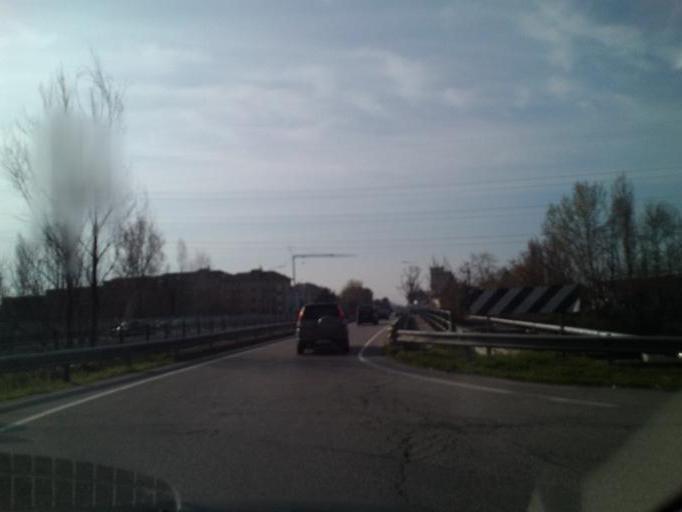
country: IT
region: Lombardy
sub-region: Provincia di Mantova
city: Sant'Antonio
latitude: 45.1850
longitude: 10.7887
